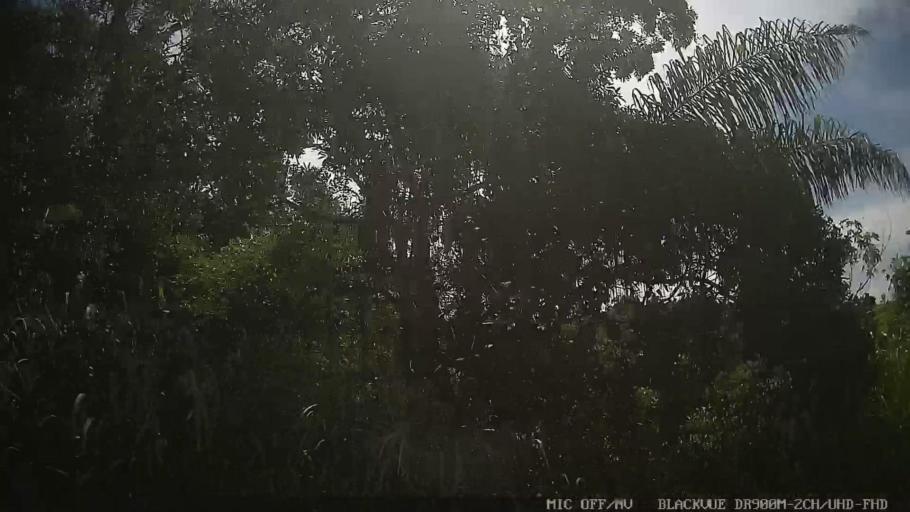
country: BR
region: Sao Paulo
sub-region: Santa Isabel
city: Santa Isabel
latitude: -23.3602
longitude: -46.1947
